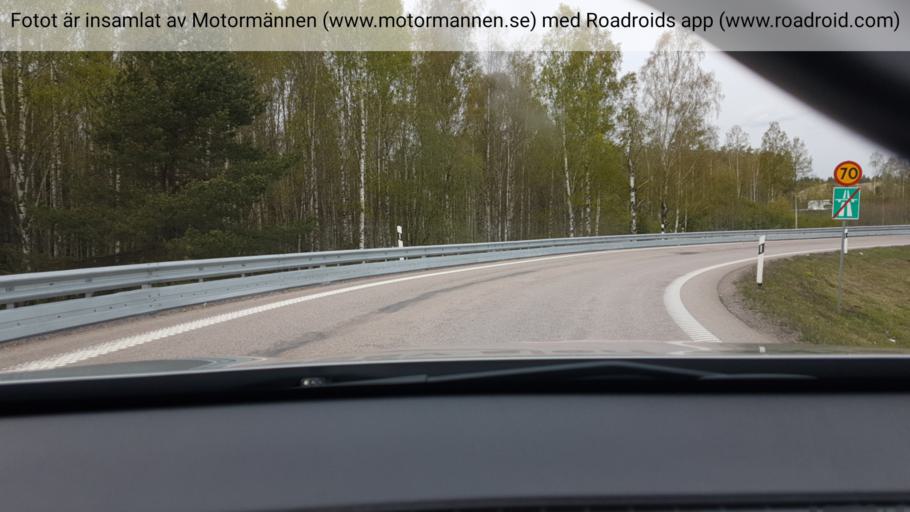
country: SE
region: Gaevleborg
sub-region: Sandvikens Kommun
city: Sandviken
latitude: 60.6252
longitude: 16.8937
